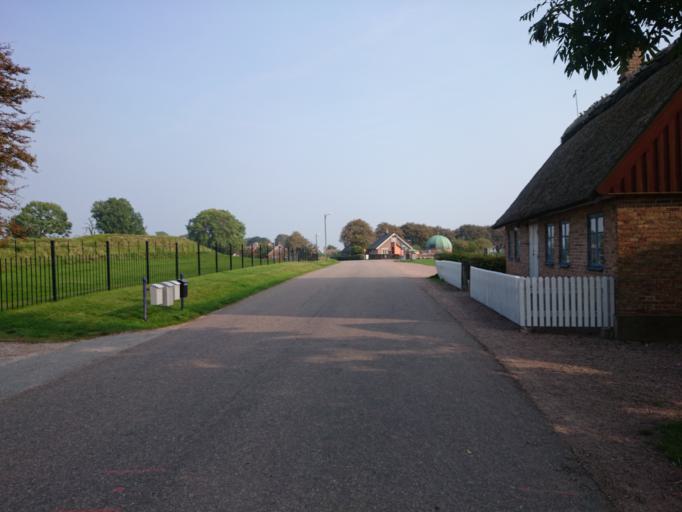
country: SE
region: Skane
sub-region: Helsingborg
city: Rydeback
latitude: 55.9074
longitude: 12.6958
